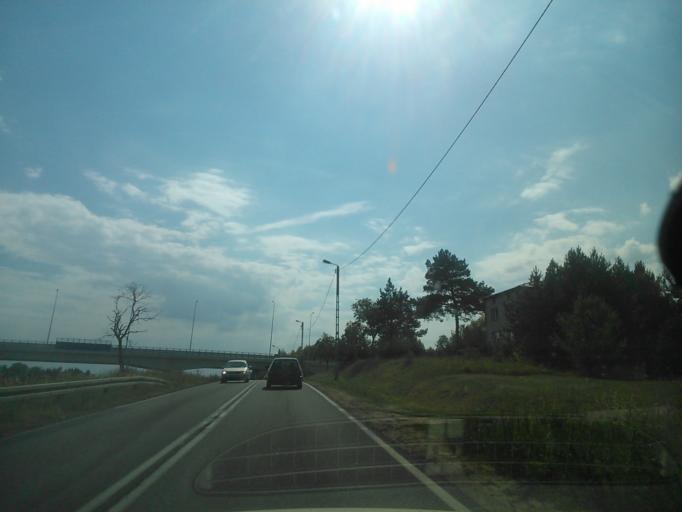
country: PL
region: Warmian-Masurian Voivodeship
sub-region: Powiat dzialdowski
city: Ilowo -Osada
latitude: 53.1429
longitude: 20.3393
